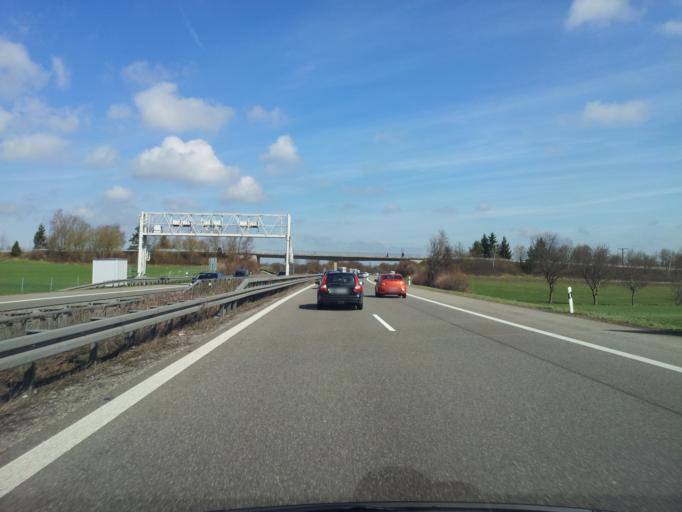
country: DE
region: Baden-Wuerttemberg
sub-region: Freiburg Region
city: Vohringen
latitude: 48.3314
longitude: 8.6465
